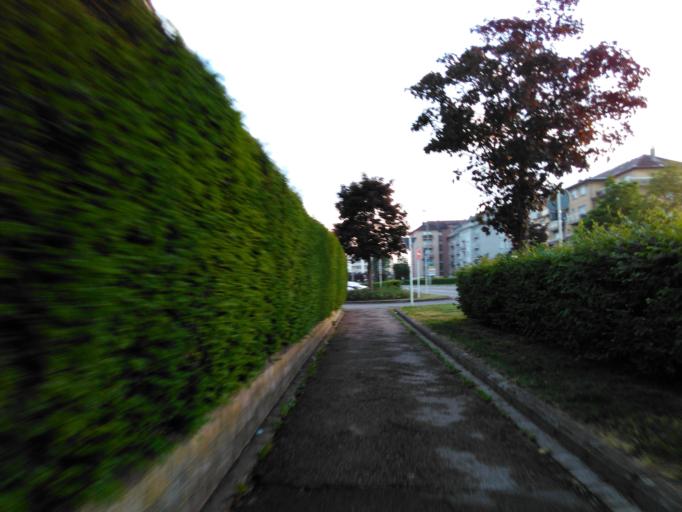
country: LU
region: Luxembourg
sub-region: Canton d'Esch-sur-Alzette
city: Esch-sur-Alzette
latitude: 49.5037
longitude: 5.9746
